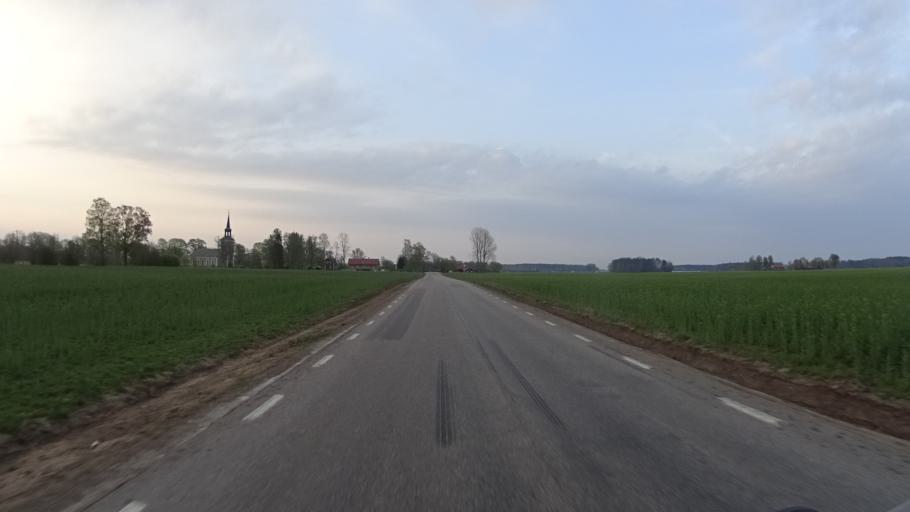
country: SE
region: Vaestra Goetaland
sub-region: Gotene Kommun
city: Kallby
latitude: 58.4755
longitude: 13.3237
